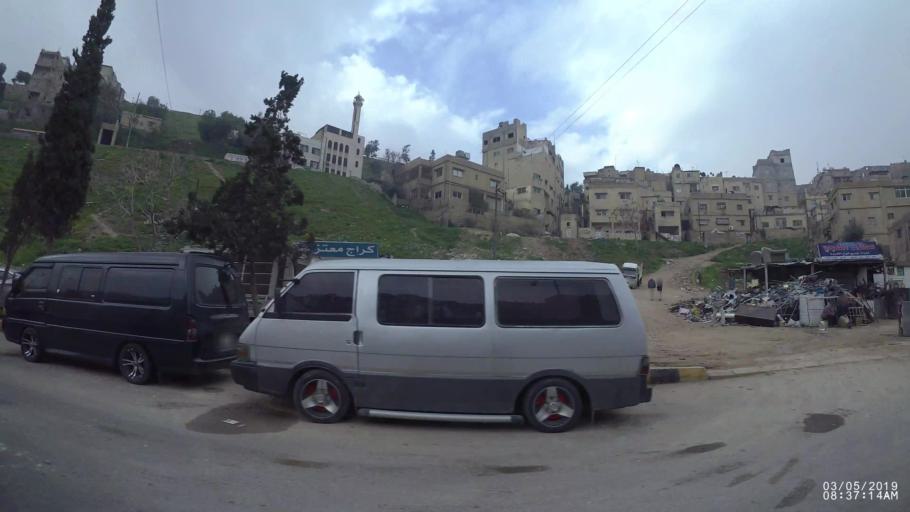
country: JO
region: Amman
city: Amman
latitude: 31.9562
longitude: 35.9378
